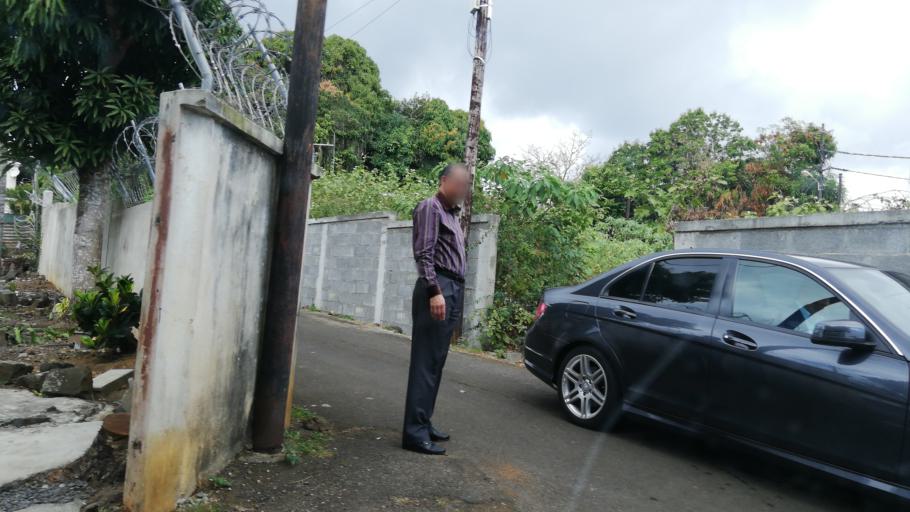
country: MU
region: Plaines Wilhems
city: Ebene
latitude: -20.2316
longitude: 57.4697
